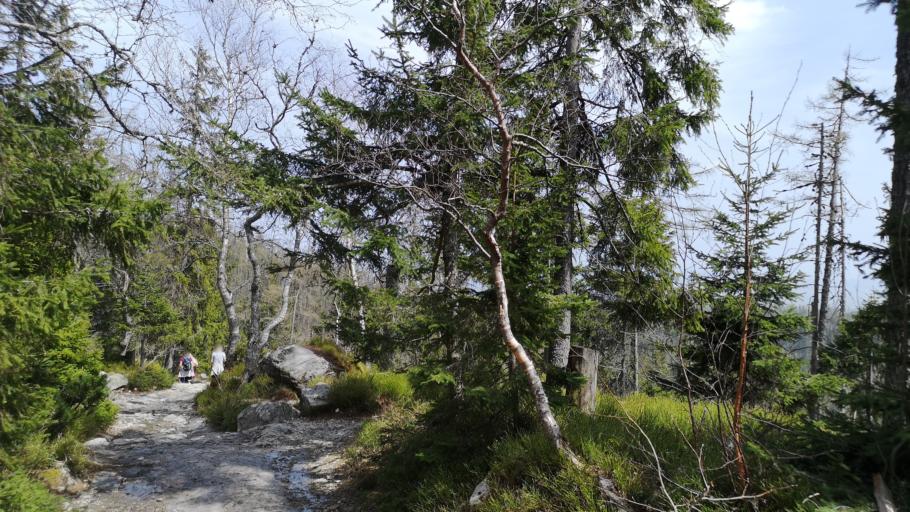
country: SK
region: Presovsky
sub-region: Okres Poprad
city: Vysoke Tatry
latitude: 49.1628
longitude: 20.2240
